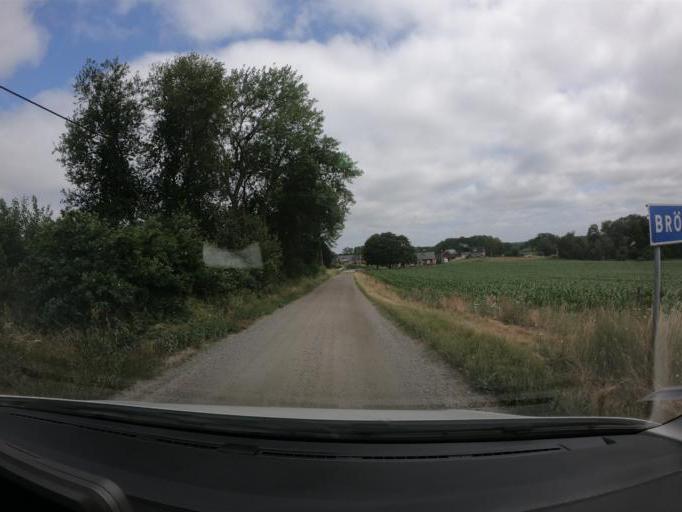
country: SE
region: Skane
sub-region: Hassleholms Kommun
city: Sosdala
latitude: 56.0799
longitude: 13.6938
